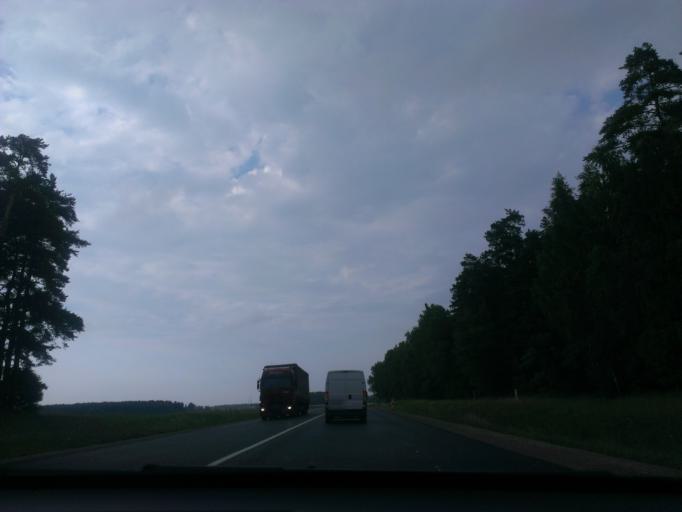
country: LV
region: Lecava
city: Iecava
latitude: 56.6421
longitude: 24.2270
